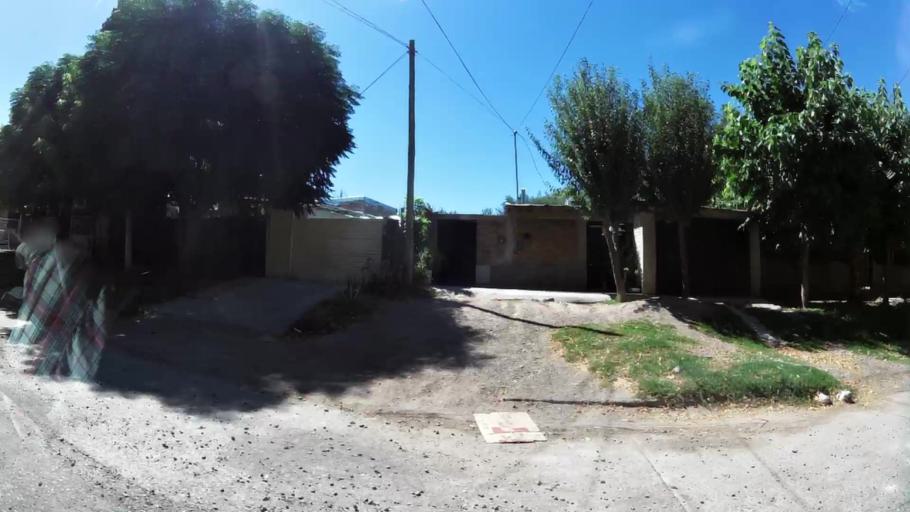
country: AR
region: Mendoza
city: Las Heras
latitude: -32.8329
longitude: -68.8445
